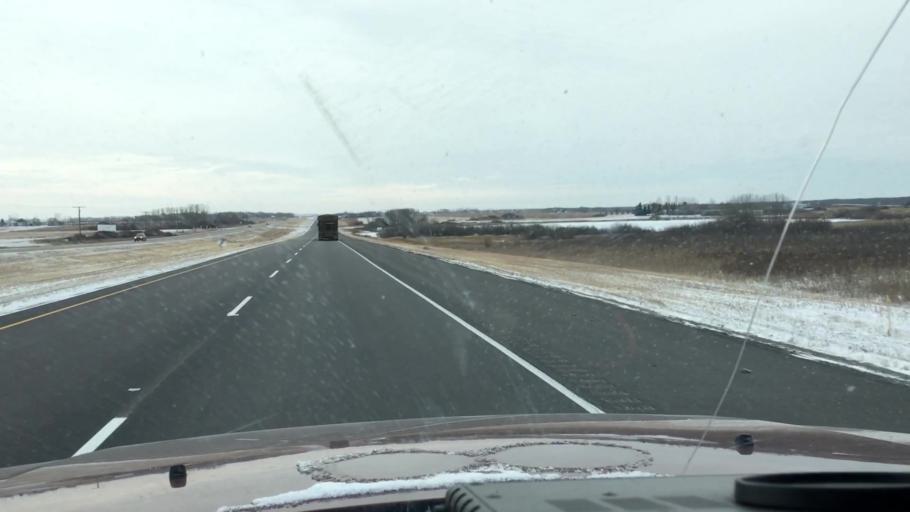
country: CA
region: Saskatchewan
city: Saskatoon
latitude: 51.9254
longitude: -106.5332
